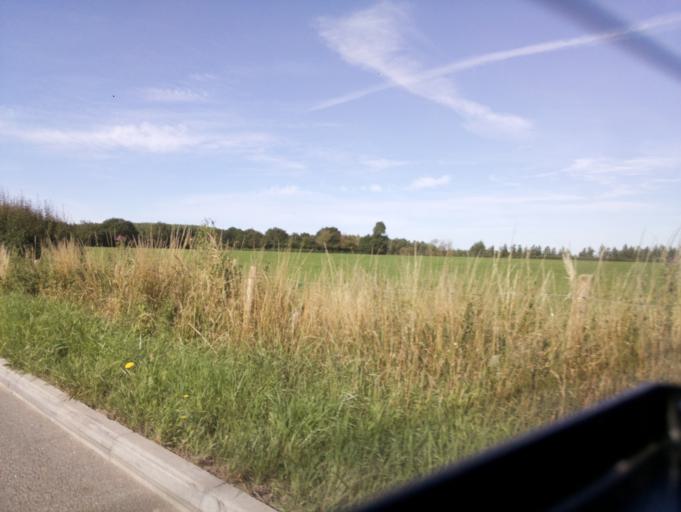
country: GB
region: England
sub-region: Bath and North East Somerset
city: Keynsham
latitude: 51.4028
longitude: -2.5164
